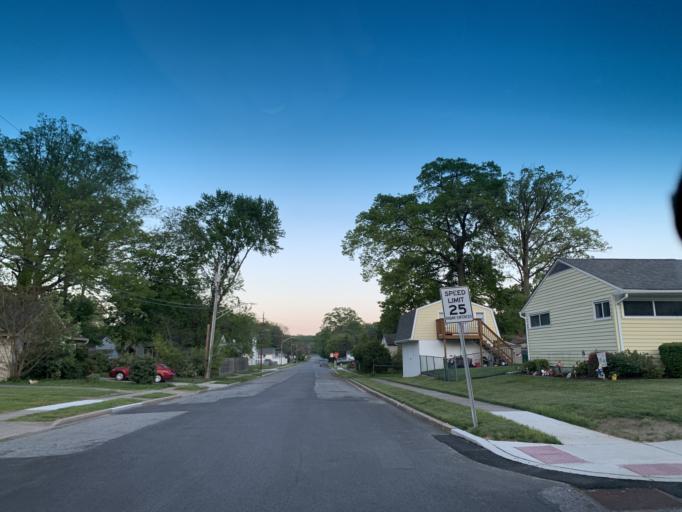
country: US
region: Maryland
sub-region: Harford County
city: Aberdeen
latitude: 39.5038
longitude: -76.1752
